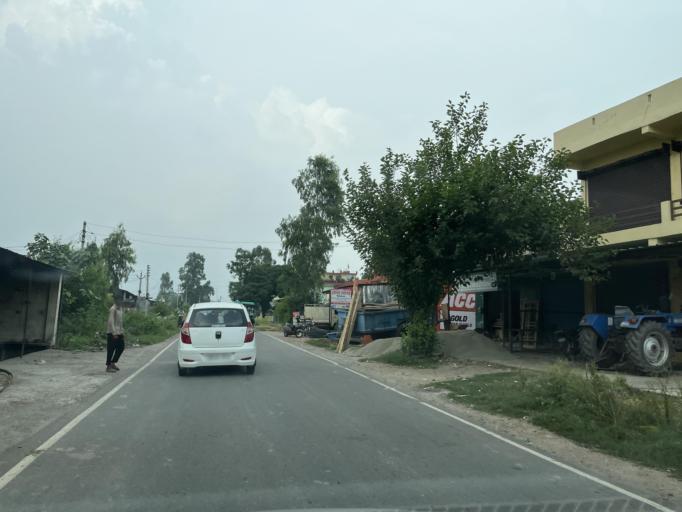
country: IN
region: Uttarakhand
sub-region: Naini Tal
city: Haldwani
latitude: 29.1830
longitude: 79.4749
